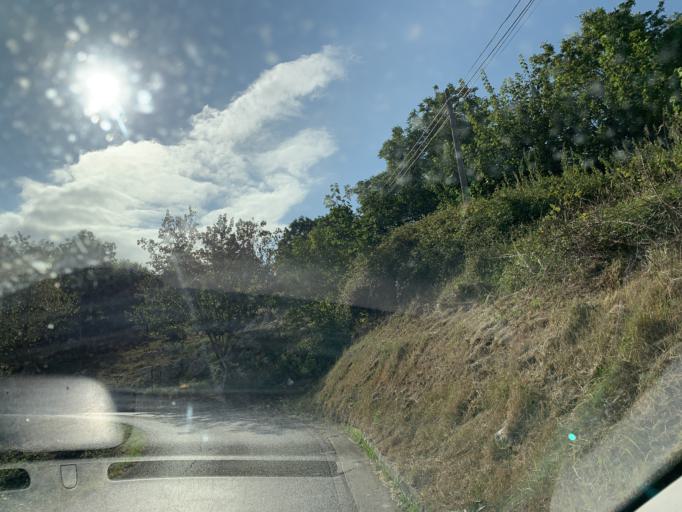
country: ES
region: Asturias
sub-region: Province of Asturias
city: Carrena
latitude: 43.3242
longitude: -4.8599
